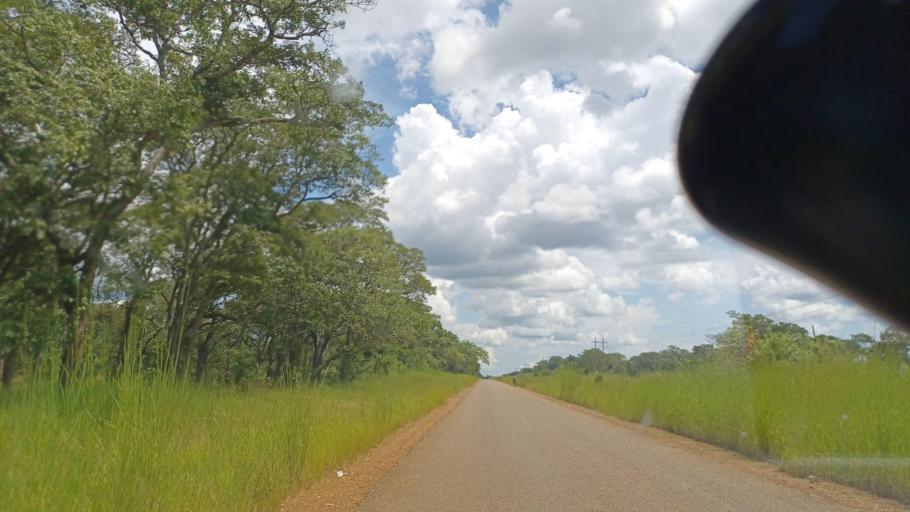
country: ZM
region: North-Western
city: Solwezi
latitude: -12.7056
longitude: 26.0312
